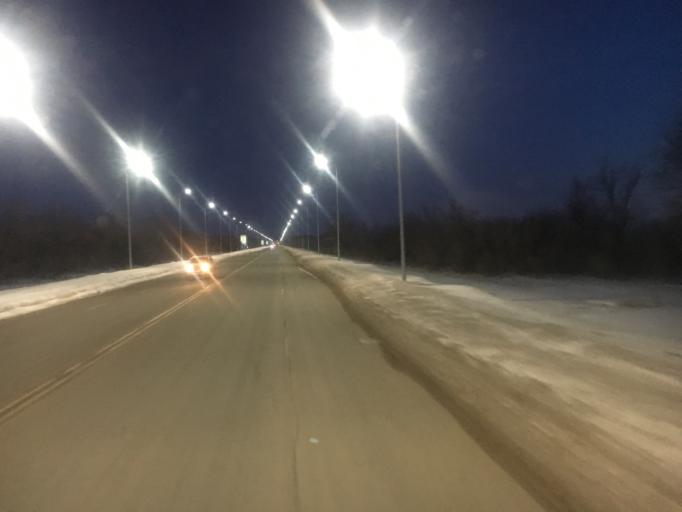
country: KZ
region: Batys Qazaqstan
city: Oral
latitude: 51.1627
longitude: 51.5271
